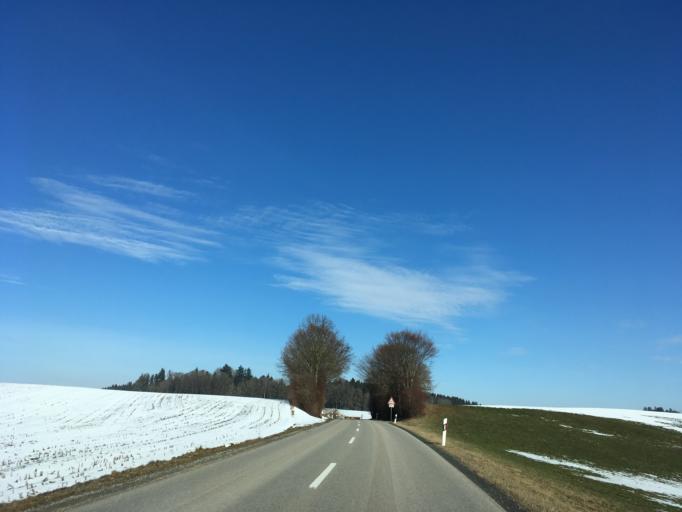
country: DE
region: Bavaria
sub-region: Upper Bavaria
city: Rechtmehring
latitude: 48.1011
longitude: 12.1607
